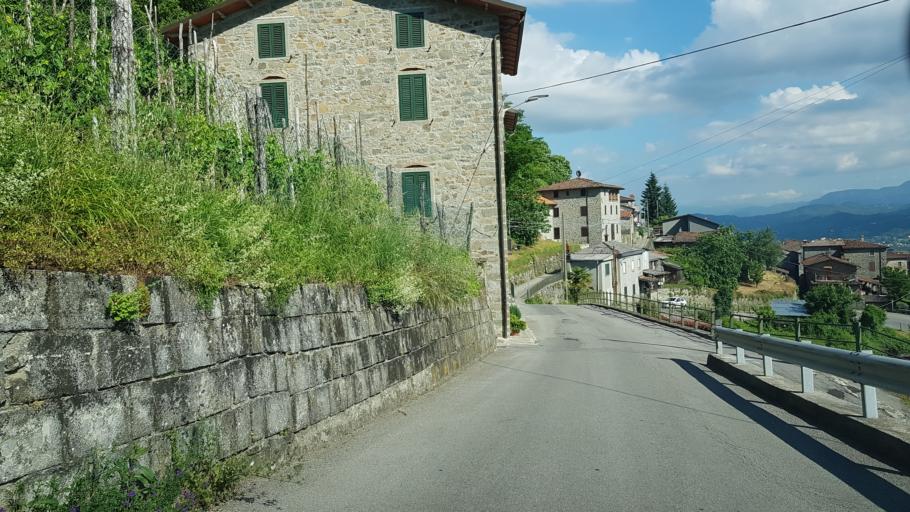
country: IT
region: Tuscany
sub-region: Provincia di Lucca
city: San Romano
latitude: 44.1721
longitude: 10.3460
